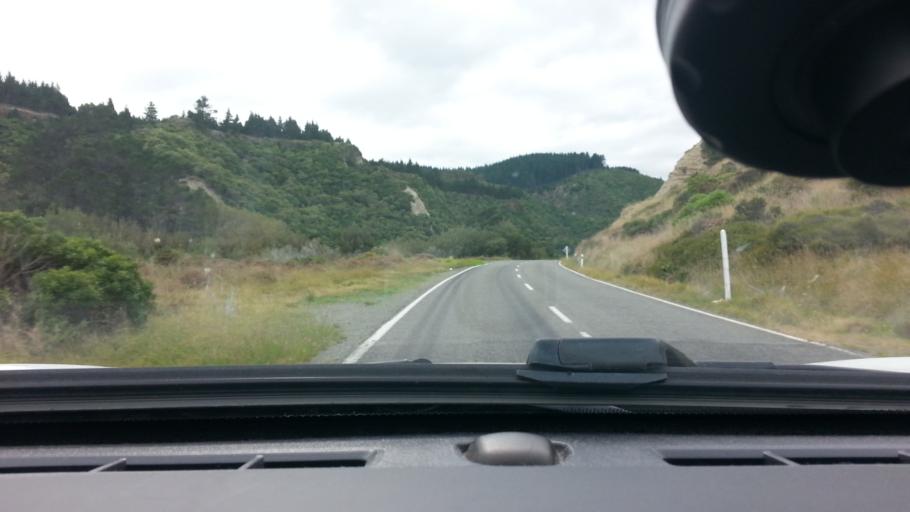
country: NZ
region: Wellington
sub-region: South Wairarapa District
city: Waipawa
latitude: -41.4420
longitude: 175.2175
